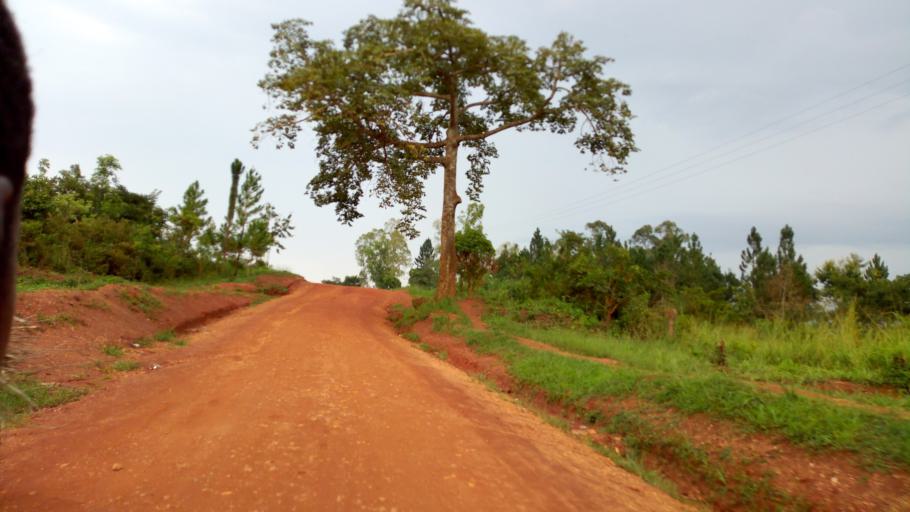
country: UG
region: Western Region
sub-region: Masindi District
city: Masindi
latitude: 1.6688
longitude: 31.7334
